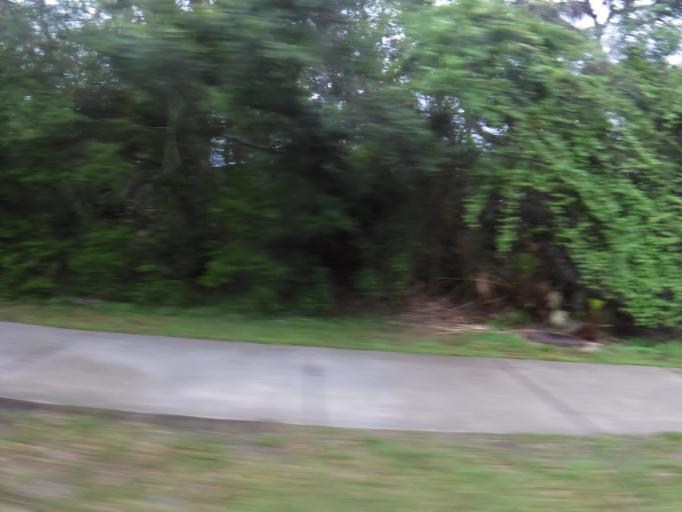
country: US
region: Florida
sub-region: Duval County
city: Atlantic Beach
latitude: 30.3581
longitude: -81.3996
